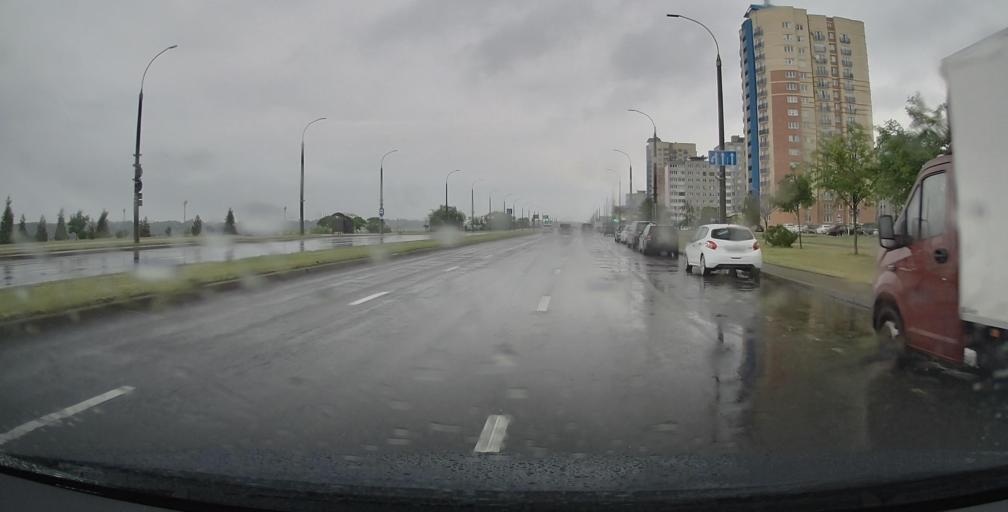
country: BY
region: Brest
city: Brest
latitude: 52.0810
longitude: 23.7429
